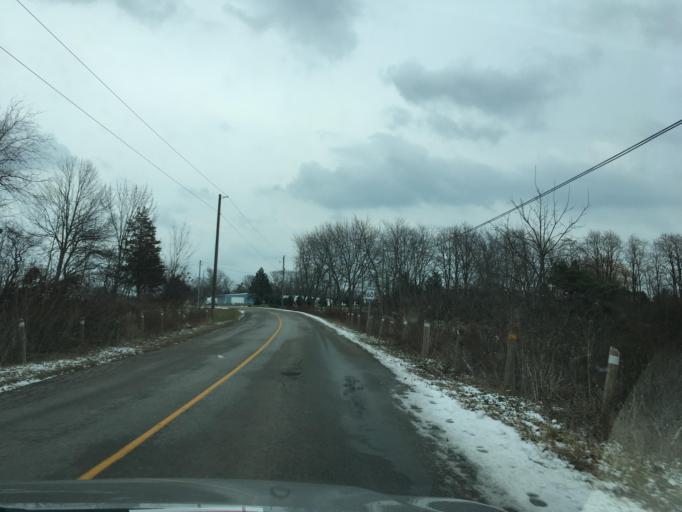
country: CA
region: Ontario
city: Norfolk County
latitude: 42.7872
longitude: -80.1592
